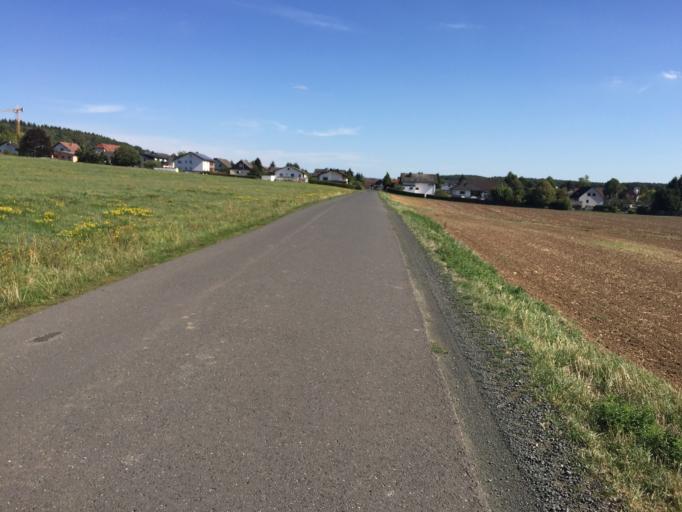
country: DE
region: Hesse
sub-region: Regierungsbezirk Giessen
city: Reiskirchen
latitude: 50.5975
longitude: 8.8504
